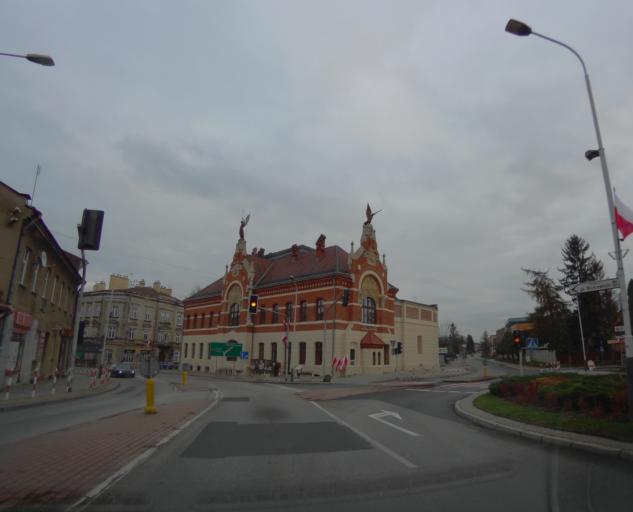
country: PL
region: Subcarpathian Voivodeship
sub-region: Powiat jaroslawski
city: Jaroslaw
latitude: 50.0167
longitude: 22.6816
